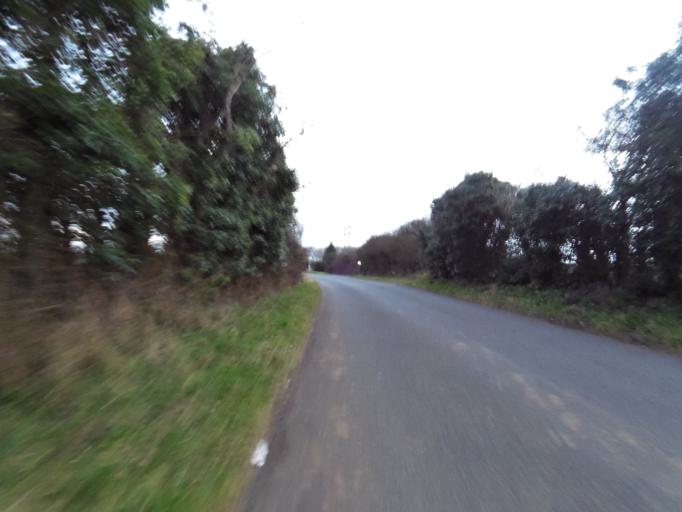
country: GB
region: England
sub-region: Essex
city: Mistley
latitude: 51.9993
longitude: 1.1124
